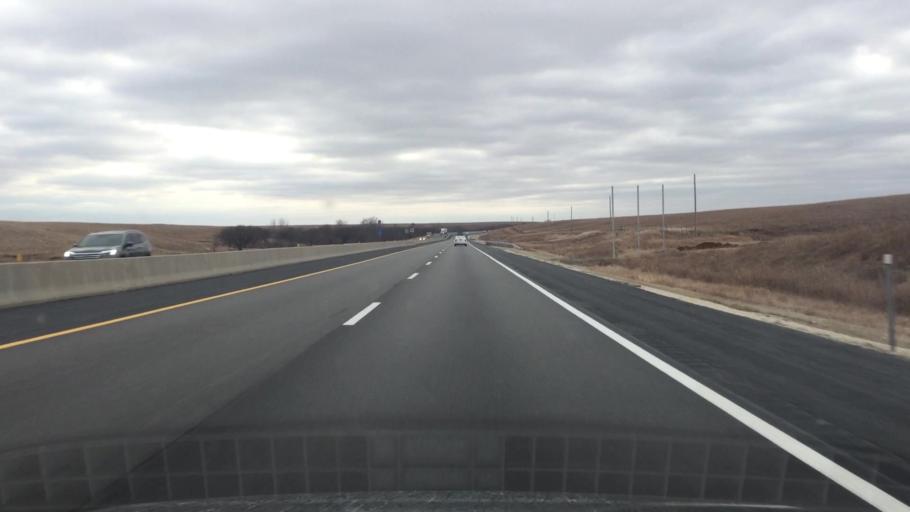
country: US
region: Kansas
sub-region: Chase County
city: Cottonwood Falls
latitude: 38.1562
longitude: -96.4892
